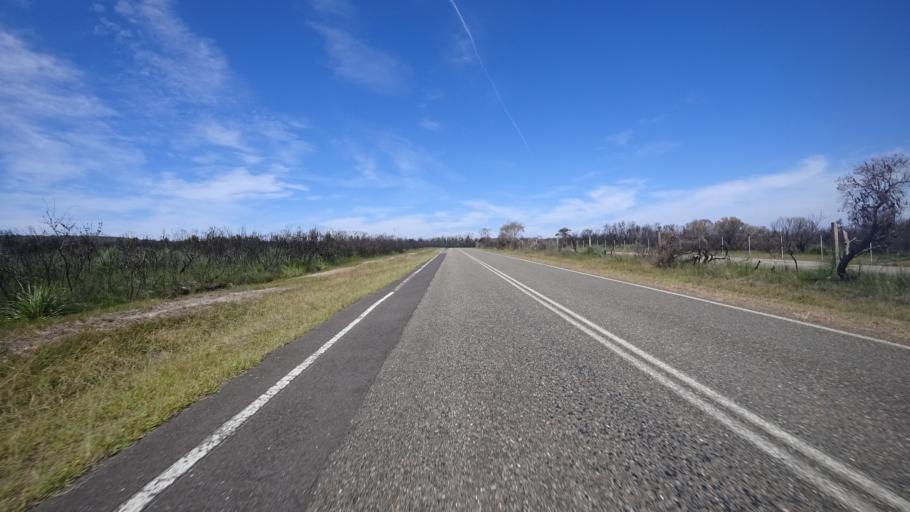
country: AU
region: New South Wales
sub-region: Shoalhaven Shire
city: Falls Creek
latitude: -35.1507
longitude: 150.7077
